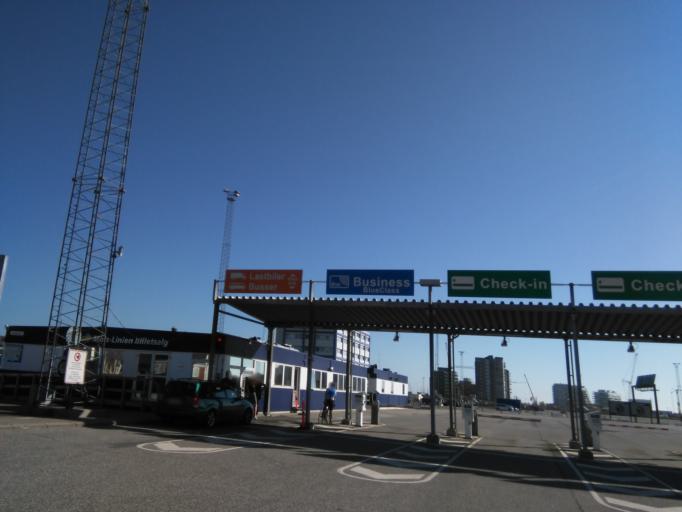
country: DK
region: Central Jutland
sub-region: Arhus Kommune
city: Arhus
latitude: 56.1617
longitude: 10.2186
